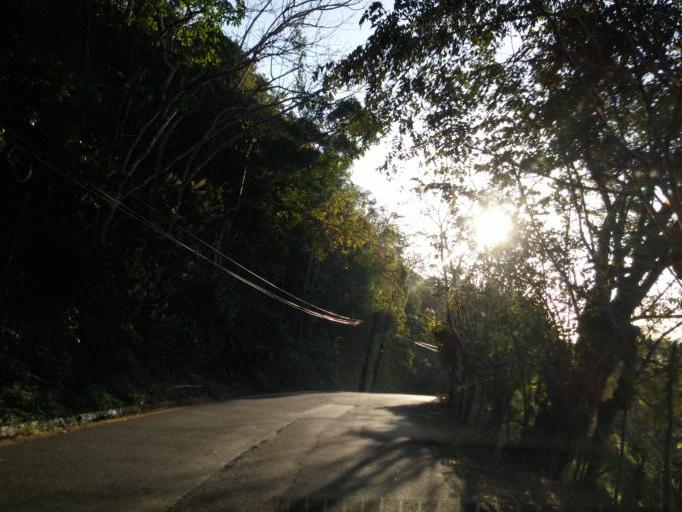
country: CR
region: Alajuela
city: Desamparados
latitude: 9.9555
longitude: -84.4794
